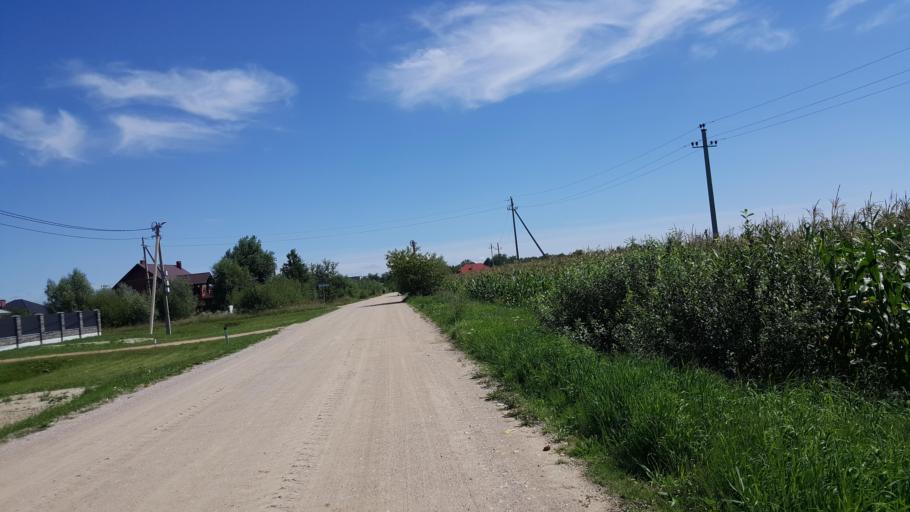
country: BY
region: Brest
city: Charnawchytsy
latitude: 52.2104
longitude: 23.7304
